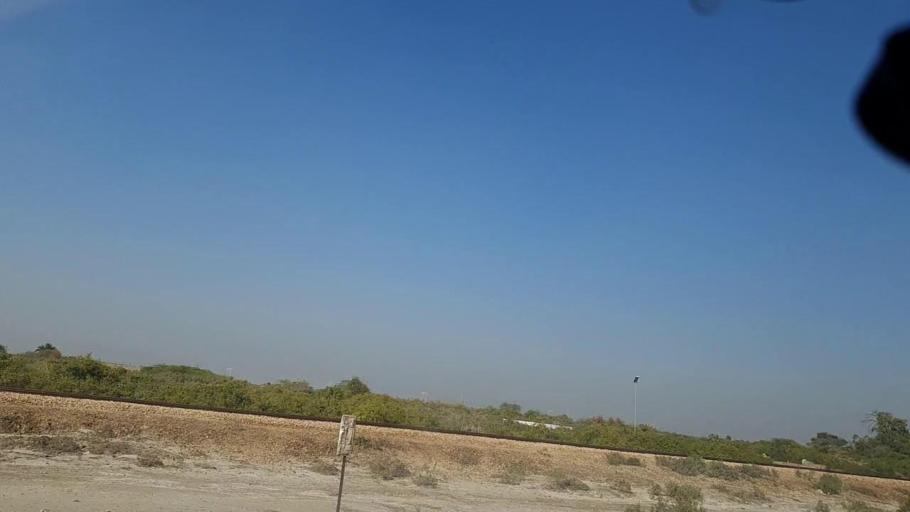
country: PK
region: Sindh
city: Mirpur Khas
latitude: 25.5128
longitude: 68.9306
